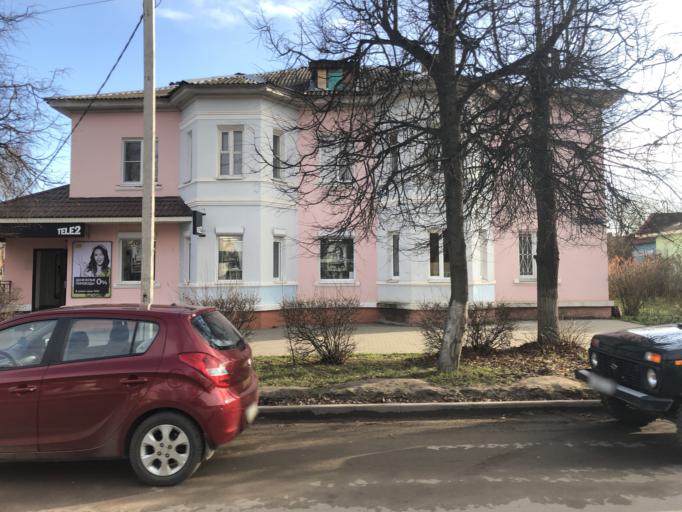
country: RU
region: Tverskaya
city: Rzhev
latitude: 56.2504
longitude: 34.3274
